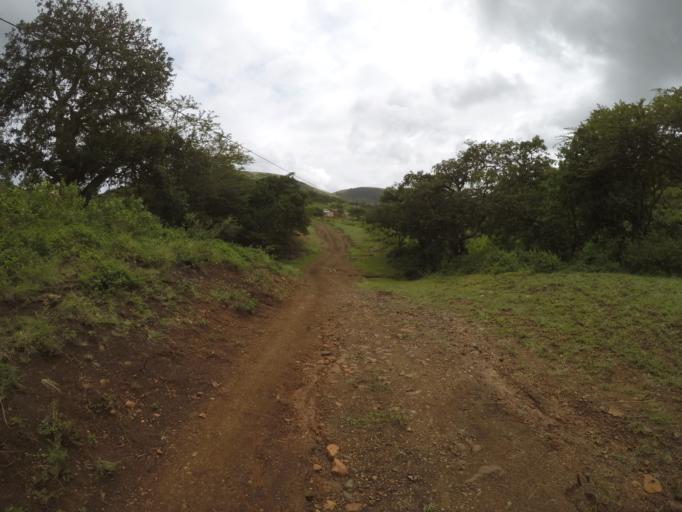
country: ZA
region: KwaZulu-Natal
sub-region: uThungulu District Municipality
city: Empangeni
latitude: -28.5835
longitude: 31.8893
